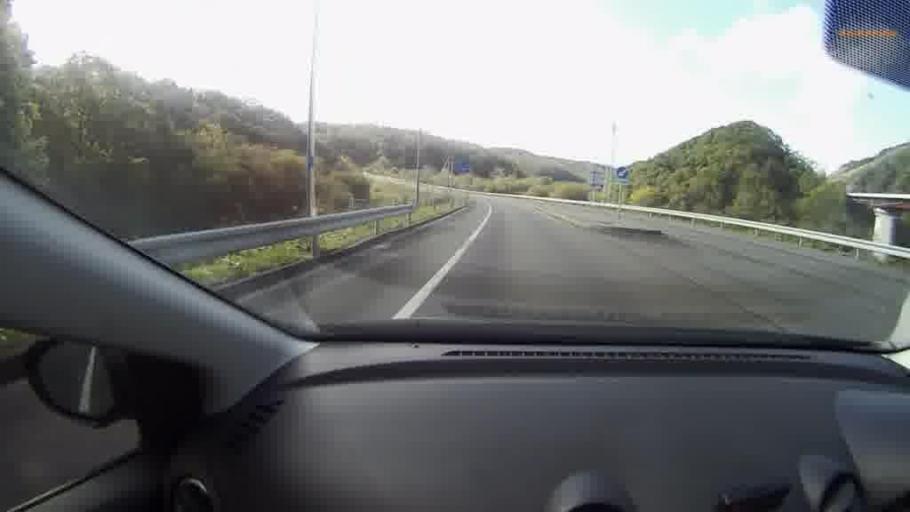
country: JP
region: Hokkaido
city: Kushiro
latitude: 43.0042
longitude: 144.5022
